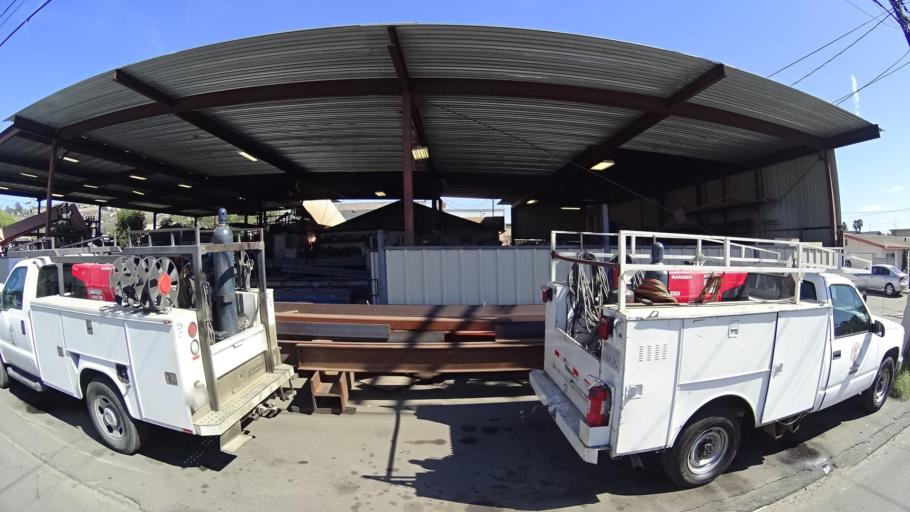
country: US
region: California
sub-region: San Diego County
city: La Presa
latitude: 32.7158
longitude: -117.0057
